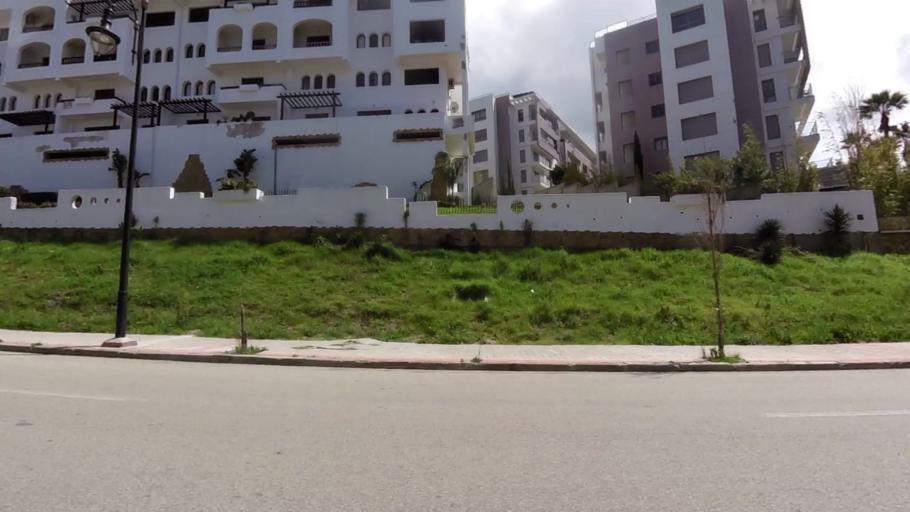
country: MA
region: Tanger-Tetouan
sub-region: Tanger-Assilah
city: Tangier
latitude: 35.7797
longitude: -5.7613
